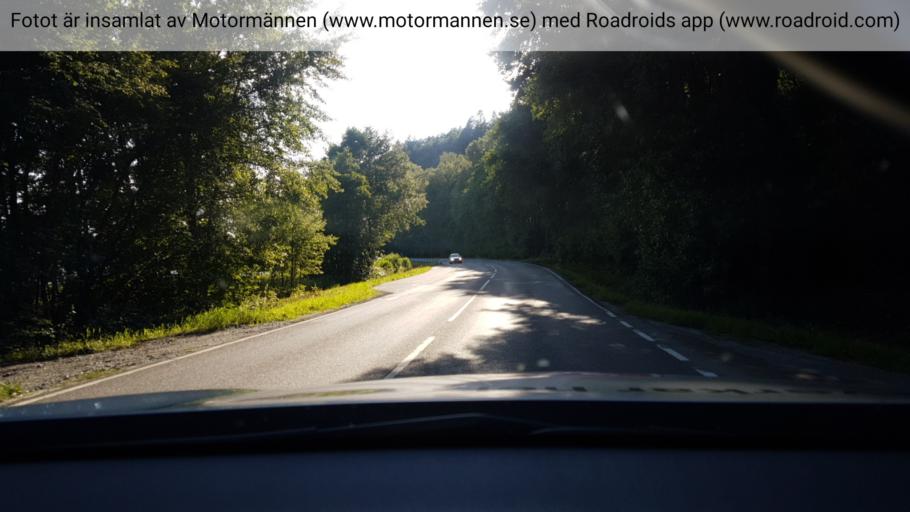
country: SE
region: Vaestra Goetaland
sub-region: Harryda Kommun
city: Landvetter
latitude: 57.6801
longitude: 12.1768
